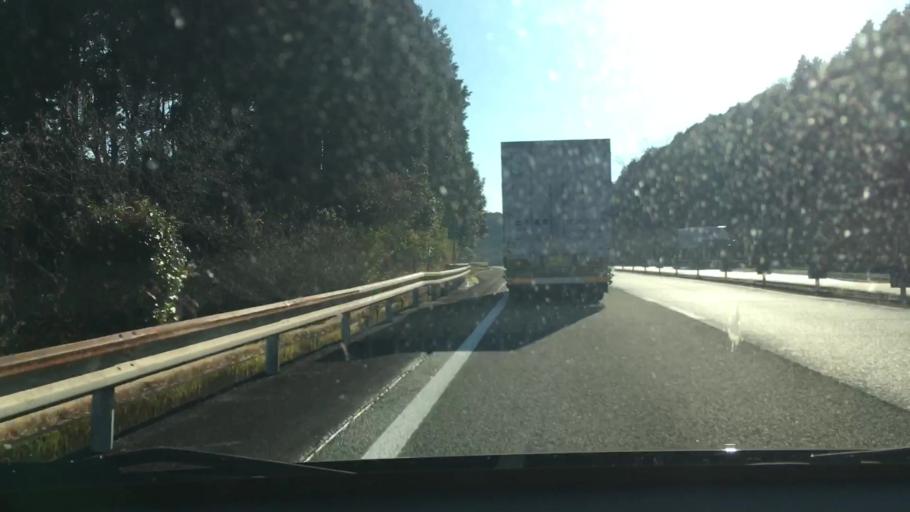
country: JP
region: Kagoshima
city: Kajiki
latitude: 31.8914
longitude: 130.6985
